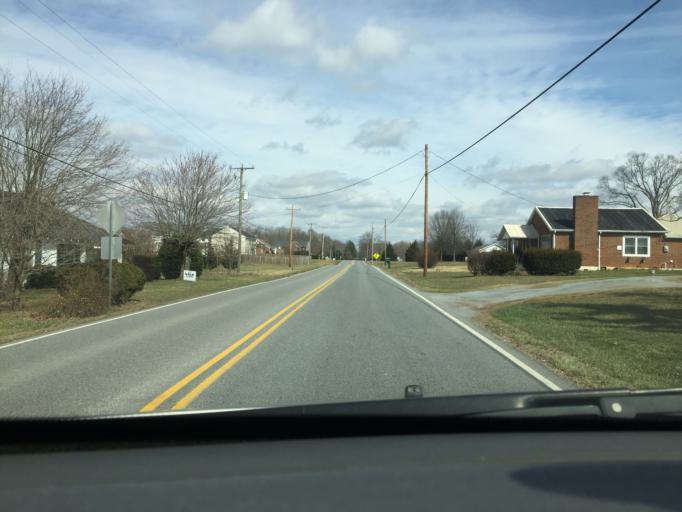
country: US
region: Virginia
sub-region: Campbell County
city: Timberlake
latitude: 37.3119
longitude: -79.3126
